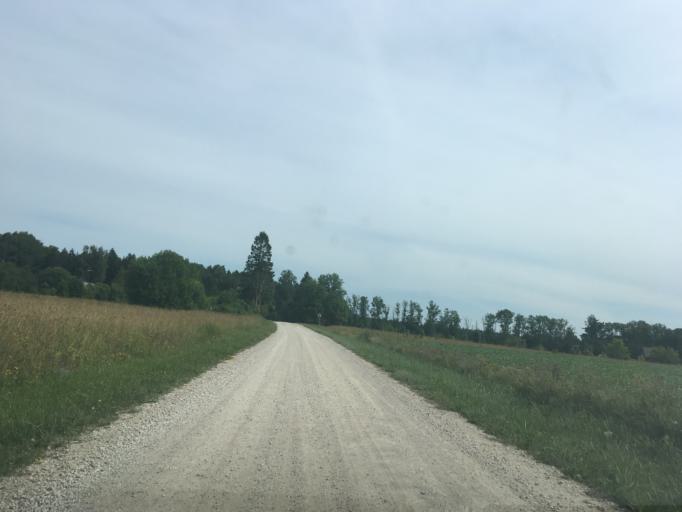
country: EE
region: Raplamaa
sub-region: Maerjamaa vald
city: Marjamaa
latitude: 58.9450
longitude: 24.5535
